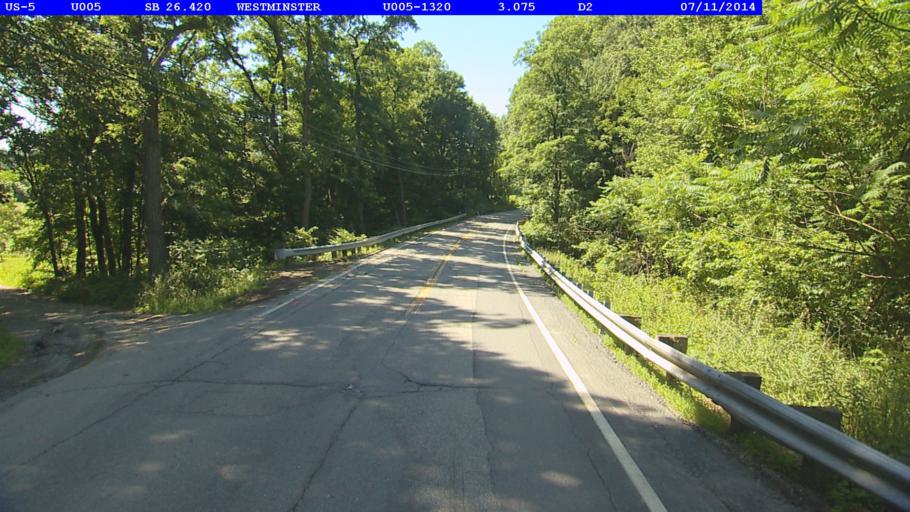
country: US
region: Vermont
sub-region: Windham County
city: Bellows Falls
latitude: 43.0621
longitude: -72.4645
